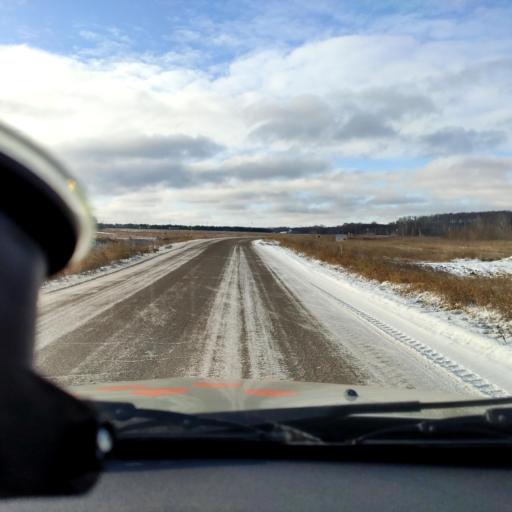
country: RU
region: Bashkortostan
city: Mikhaylovka
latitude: 54.7964
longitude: 55.7765
